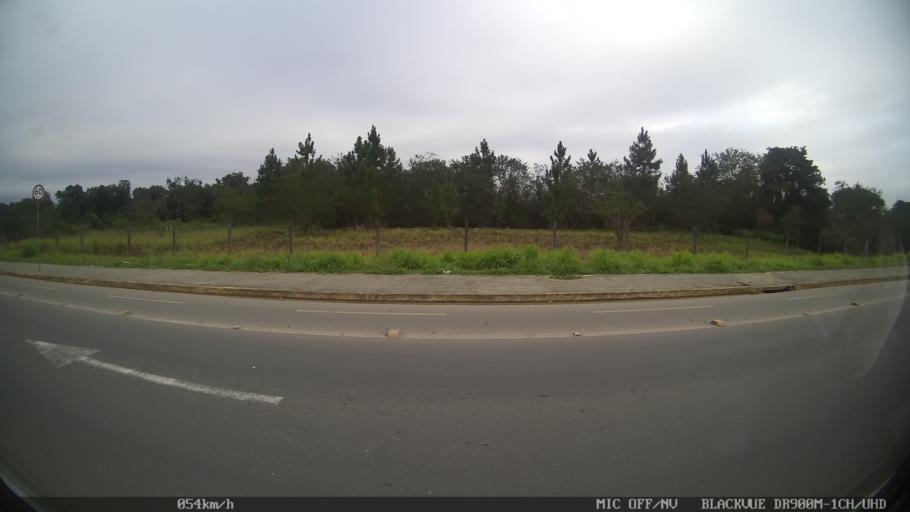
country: BR
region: Santa Catarina
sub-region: Joinville
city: Joinville
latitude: -26.3376
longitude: -48.8926
